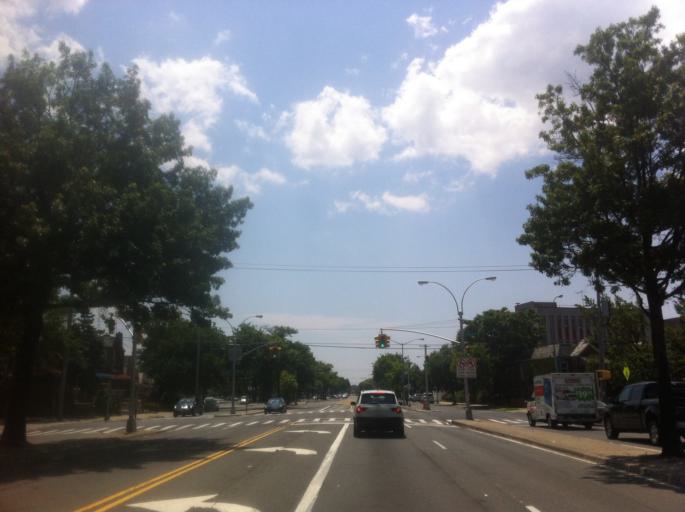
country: US
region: New York
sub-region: Kings County
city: Brooklyn
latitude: 40.6490
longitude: -73.9242
